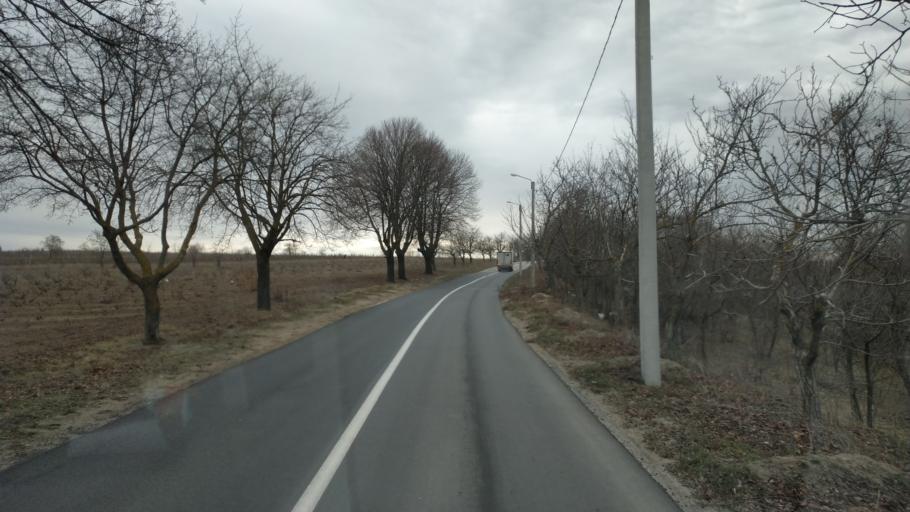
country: MD
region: Telenesti
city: Cocieri
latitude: 47.3354
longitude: 29.0980
